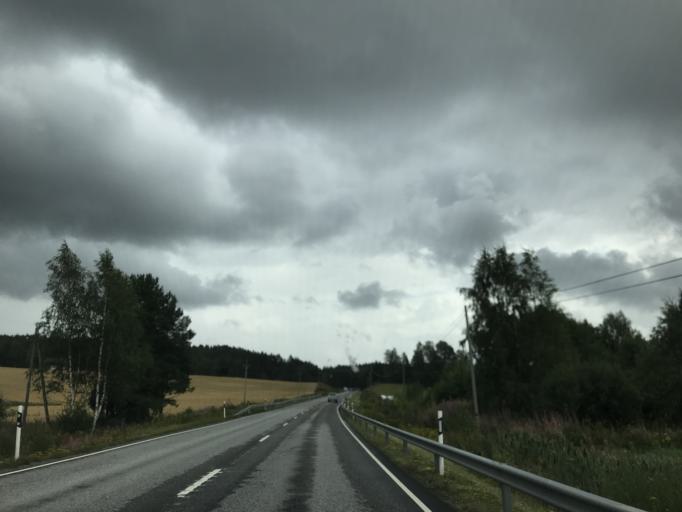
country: FI
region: Varsinais-Suomi
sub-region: Salo
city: Pernioe
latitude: 60.0897
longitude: 23.2270
